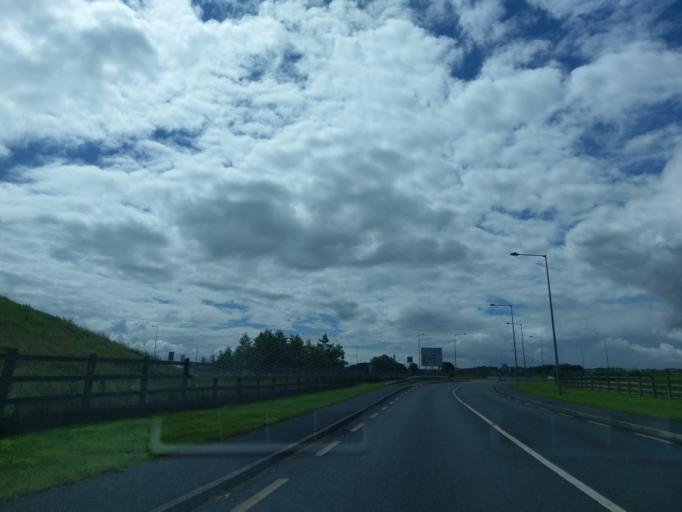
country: IE
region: Connaught
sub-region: County Galway
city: Athenry
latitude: 53.2946
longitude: -8.7591
